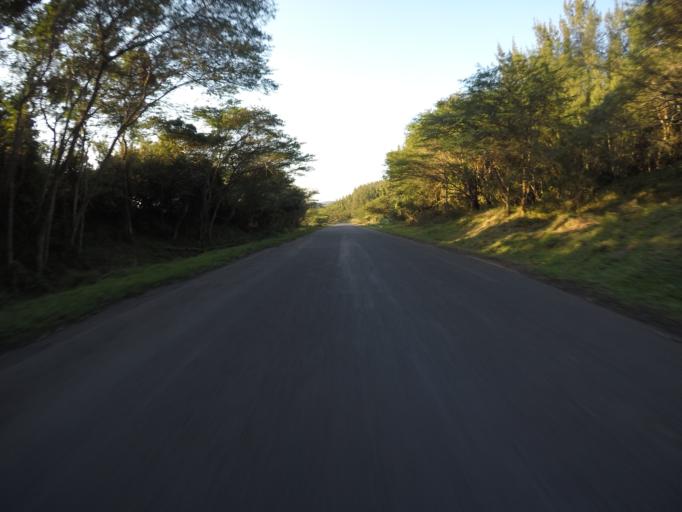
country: ZA
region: KwaZulu-Natal
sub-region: uThungulu District Municipality
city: KwaMbonambi
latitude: -28.6962
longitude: 32.2093
